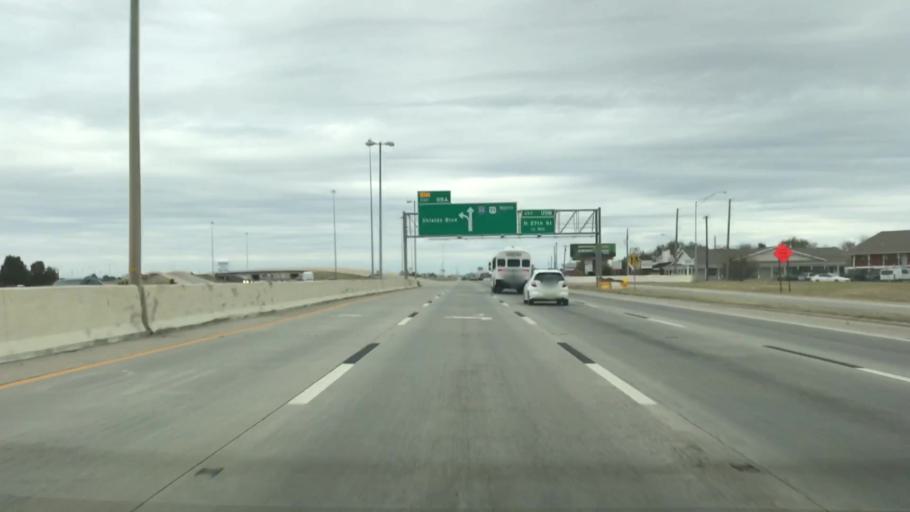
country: US
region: Oklahoma
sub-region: Cleveland County
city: Moore
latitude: 35.3529
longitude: -97.4946
